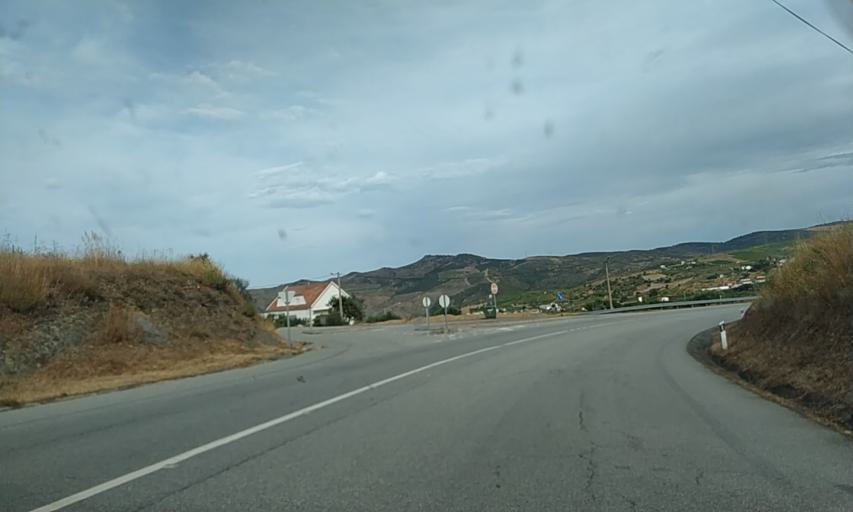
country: PT
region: Viseu
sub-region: Sao Joao da Pesqueira
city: Sao Joao da Pesqueira
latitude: 41.1034
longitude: -7.3837
